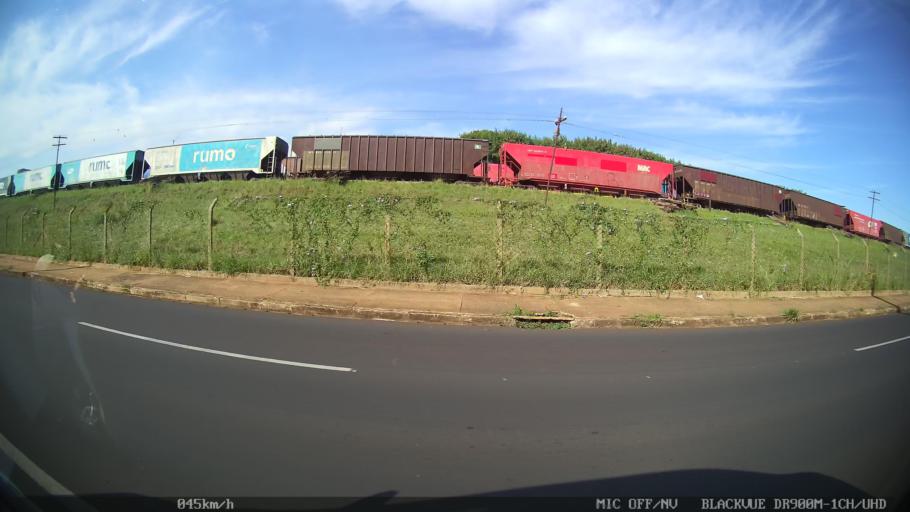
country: BR
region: Sao Paulo
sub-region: Araraquara
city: Araraquara
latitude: -21.7836
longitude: -48.1718
